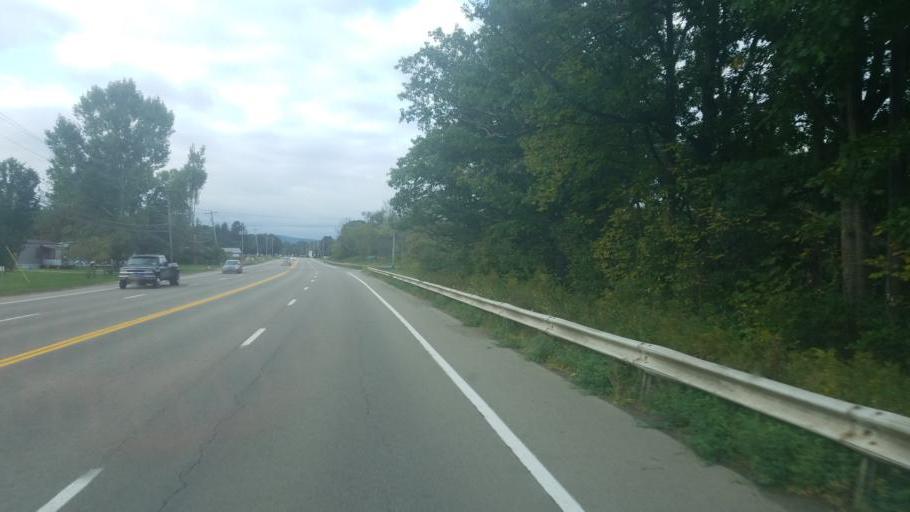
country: US
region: New York
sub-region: Cattaraugus County
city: Olean
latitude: 42.1303
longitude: -78.4094
